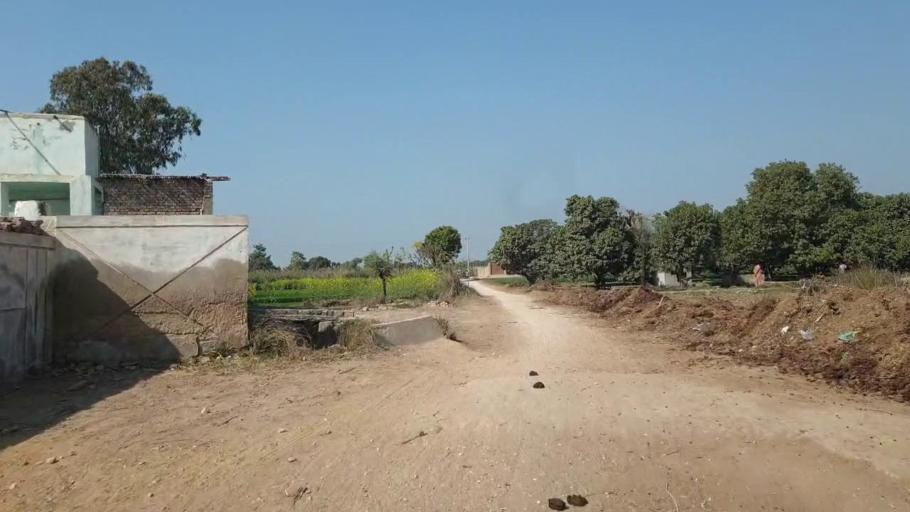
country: PK
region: Sindh
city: Hala
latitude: 25.9103
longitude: 68.4311
